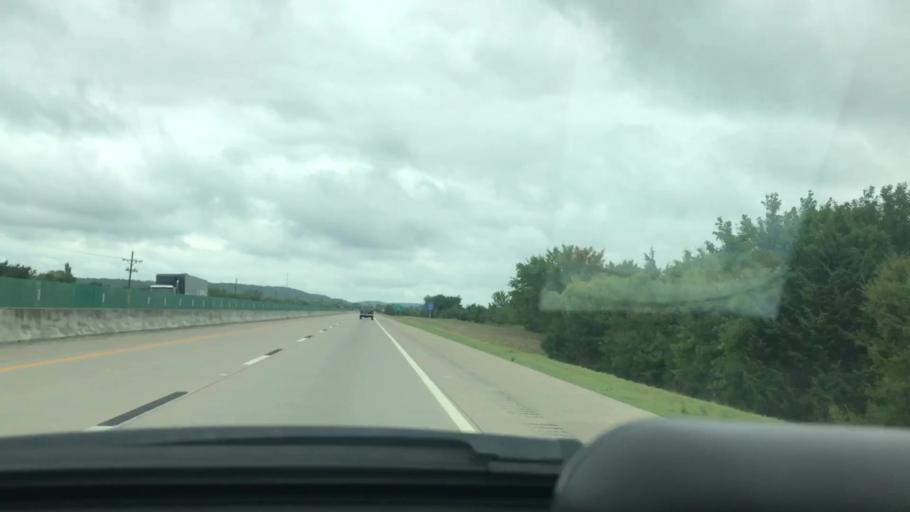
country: US
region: Oklahoma
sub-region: Pittsburg County
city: Krebs
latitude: 35.0368
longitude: -95.7122
